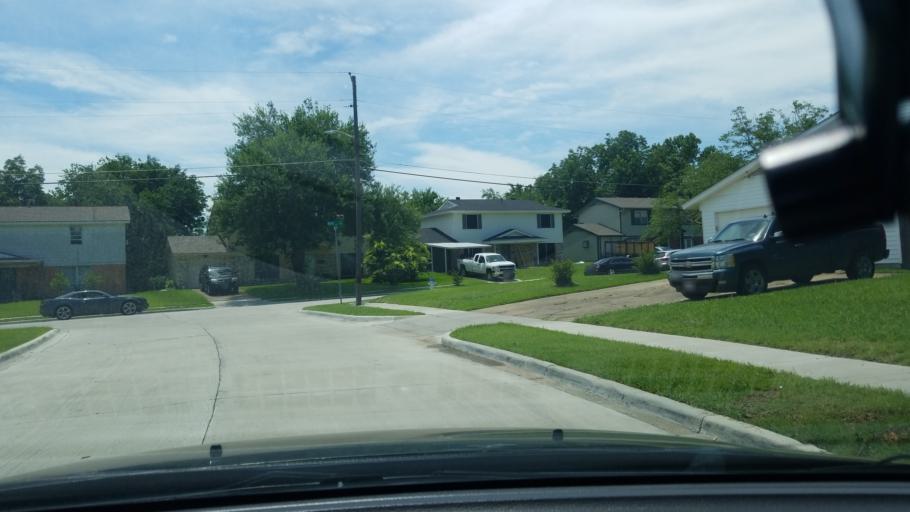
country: US
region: Texas
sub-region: Dallas County
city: Mesquite
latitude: 32.8046
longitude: -96.6552
